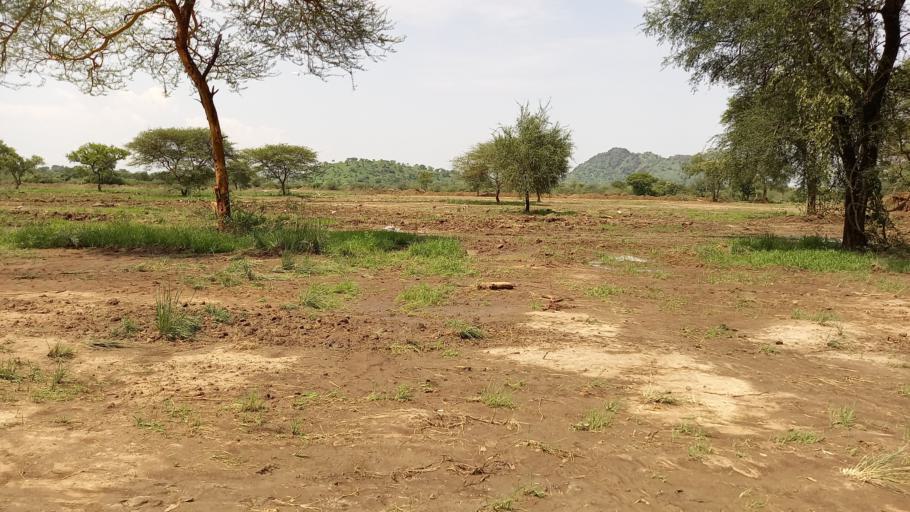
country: ET
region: Gambela
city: Gambela
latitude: 8.2856
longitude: 34.2117
